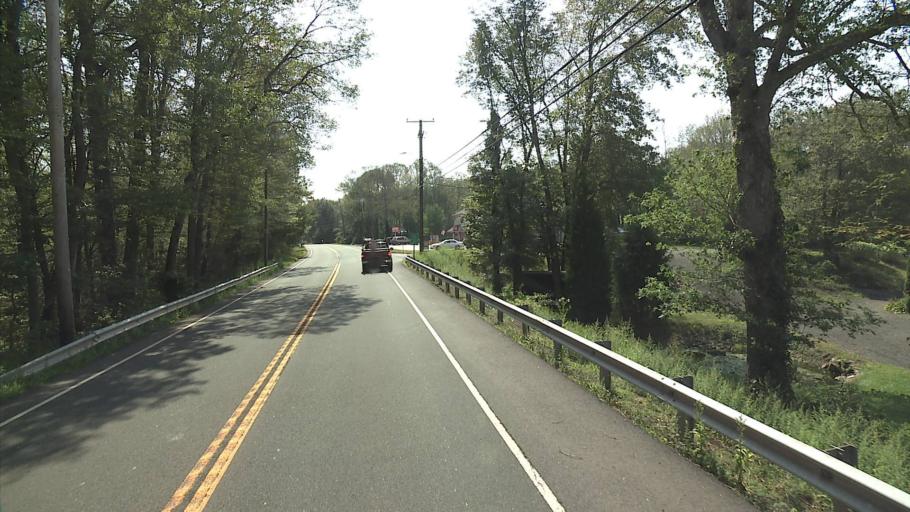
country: US
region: Connecticut
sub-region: Middlesex County
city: Durham
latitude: 41.4451
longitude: -72.6627
